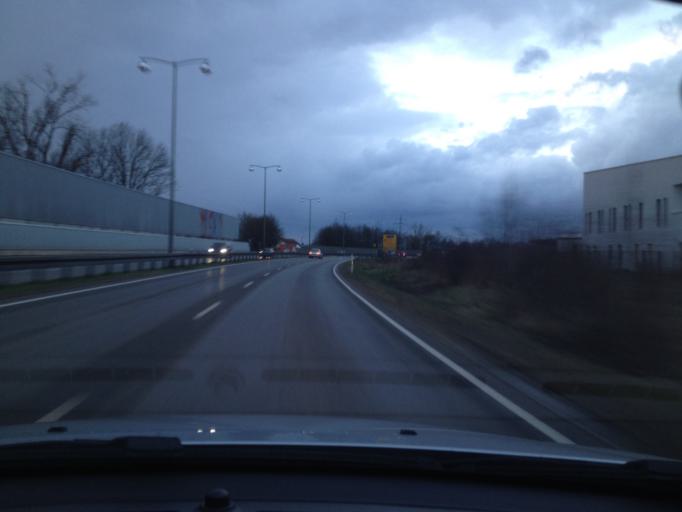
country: DE
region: Bavaria
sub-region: Swabia
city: Stadtbergen
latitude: 48.3561
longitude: 10.8517
